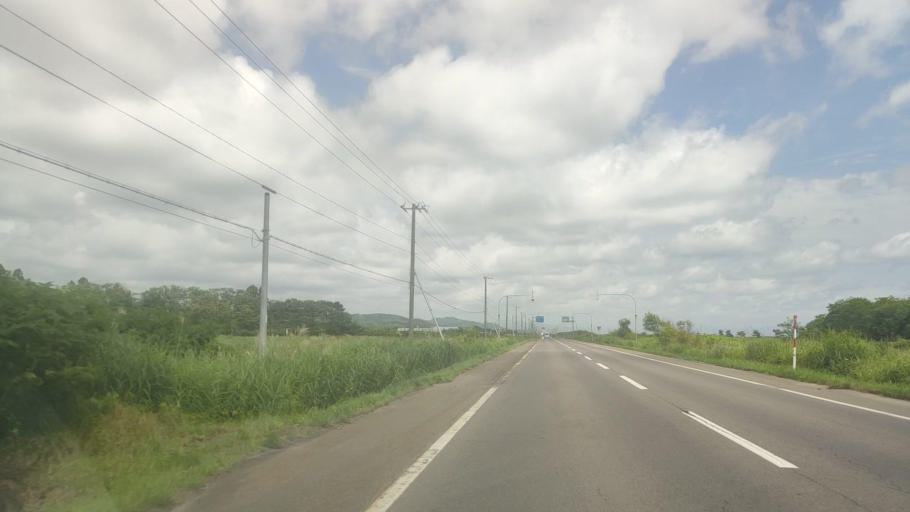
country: JP
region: Hokkaido
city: Niseko Town
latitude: 42.3902
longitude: 140.2981
